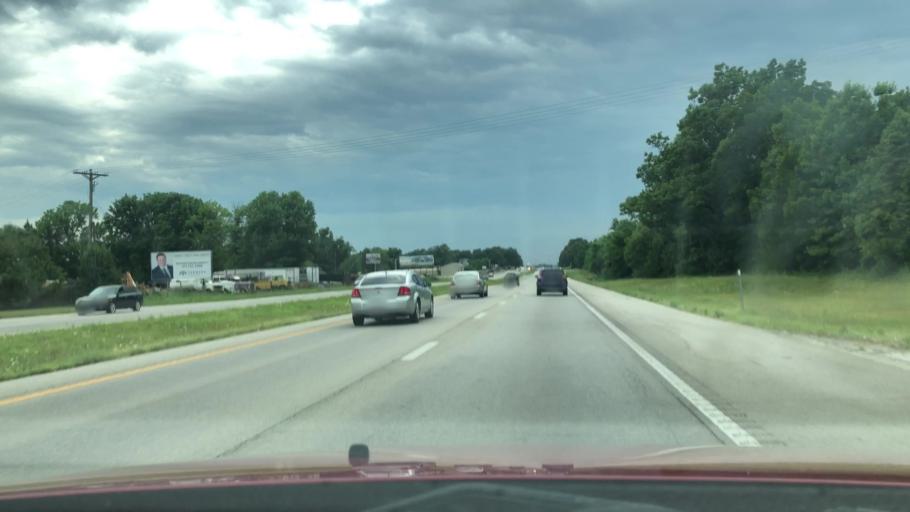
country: US
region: Missouri
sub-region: Greene County
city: Republic
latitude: 37.1415
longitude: -93.4382
